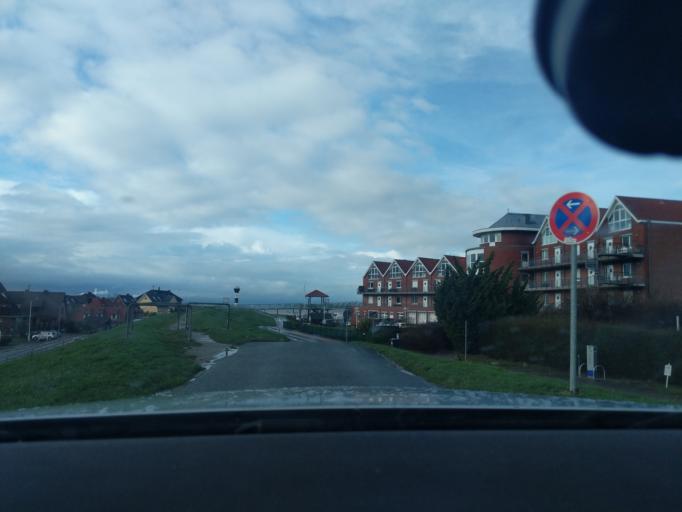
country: DE
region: Schleswig-Holstein
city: Haseldorf
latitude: 53.6024
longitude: 9.5602
